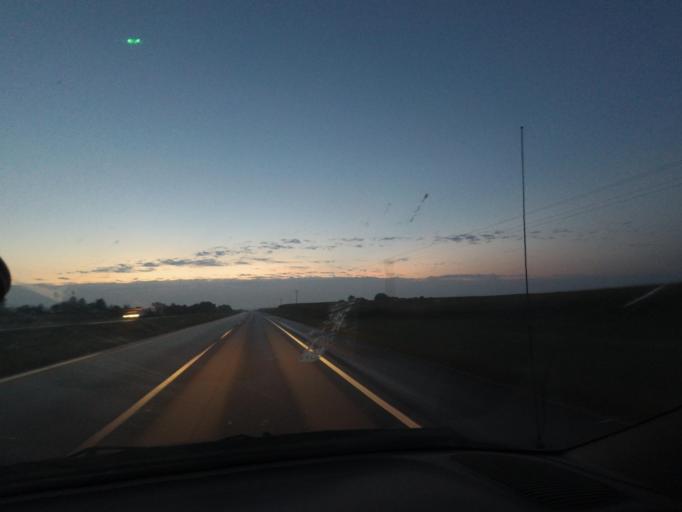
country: US
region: Missouri
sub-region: Linn County
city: Linneus
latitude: 39.7777
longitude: -93.2571
